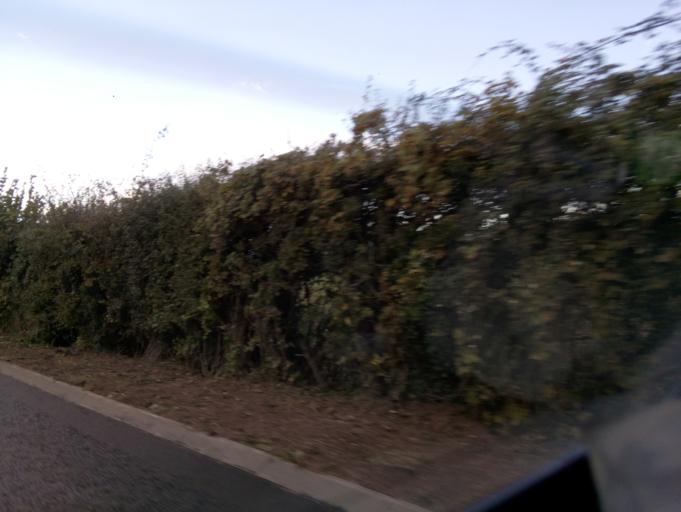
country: GB
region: England
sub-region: Herefordshire
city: Ocle Pychard
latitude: 52.0649
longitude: -2.5644
